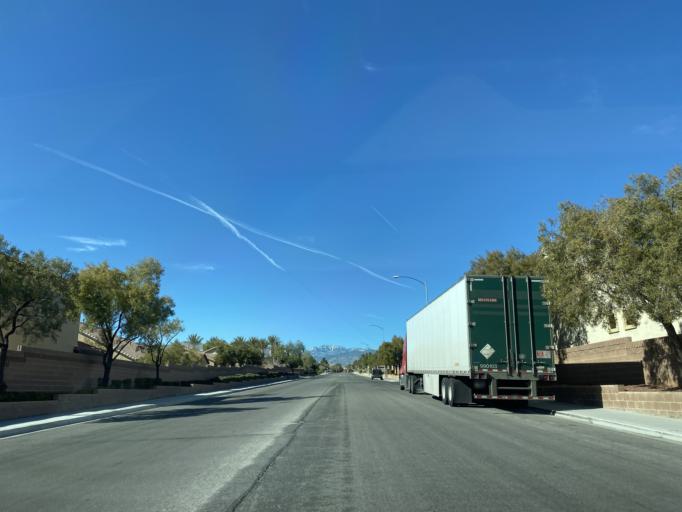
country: US
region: Nevada
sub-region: Clark County
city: Summerlin South
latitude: 36.3031
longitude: -115.3103
